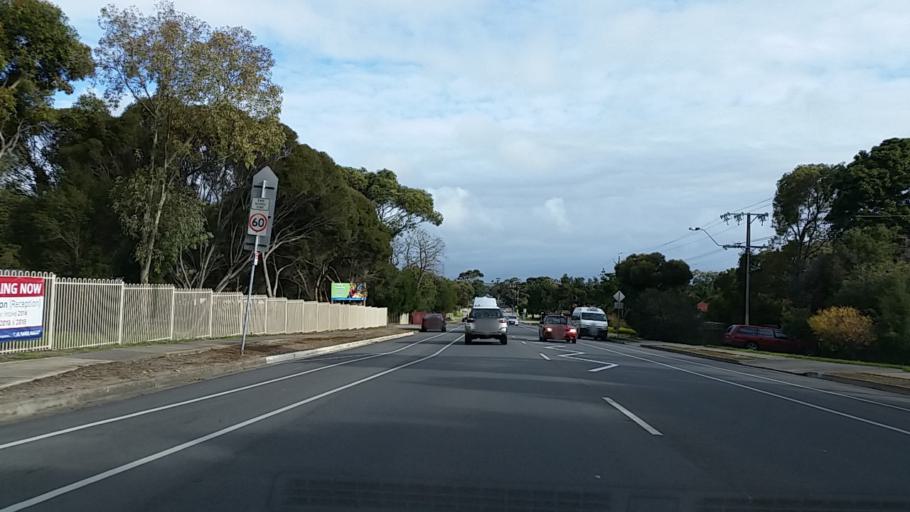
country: AU
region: South Australia
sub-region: Onkaparinga
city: Reynella
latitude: -35.1123
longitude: 138.5354
